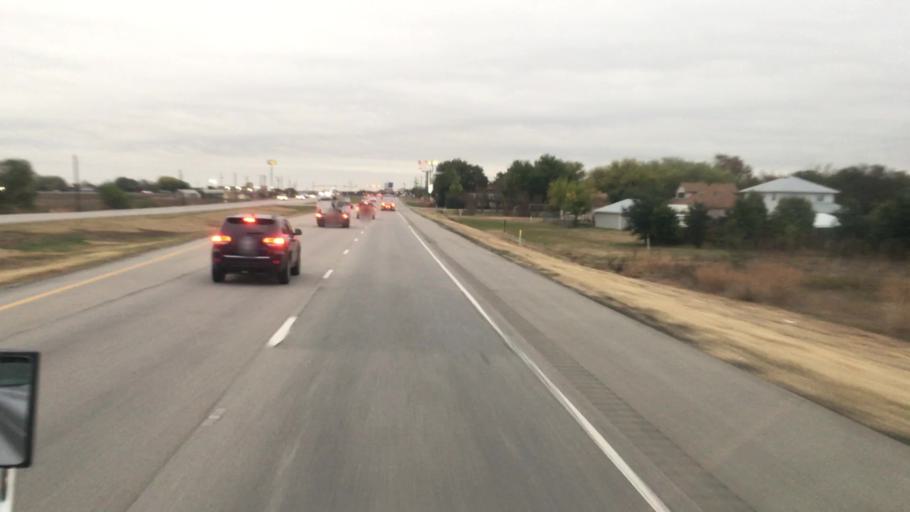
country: US
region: Texas
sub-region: Johnson County
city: Venus
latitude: 32.4352
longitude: -97.1106
